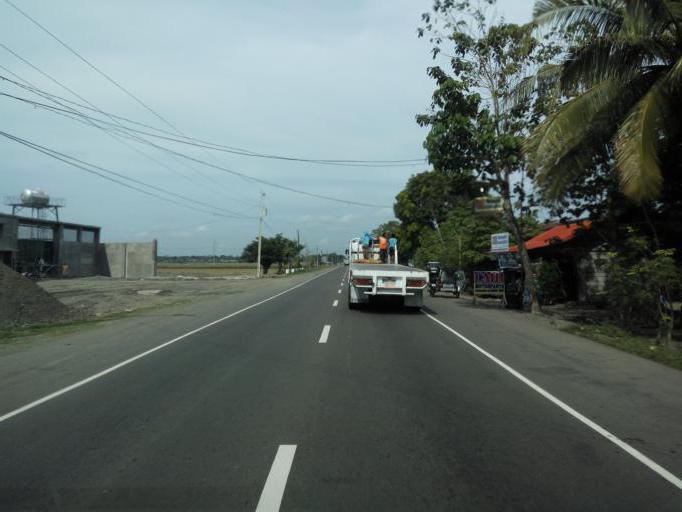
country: PH
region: Cagayan Valley
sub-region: Province of Isabela
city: Reina Mercedes
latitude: 17.0029
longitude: 121.8243
